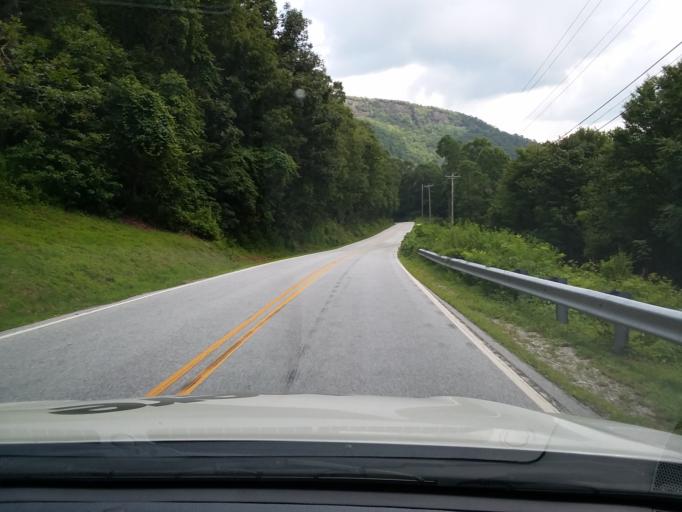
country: US
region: Georgia
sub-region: Rabun County
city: Mountain City
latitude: 35.0268
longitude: -83.2925
